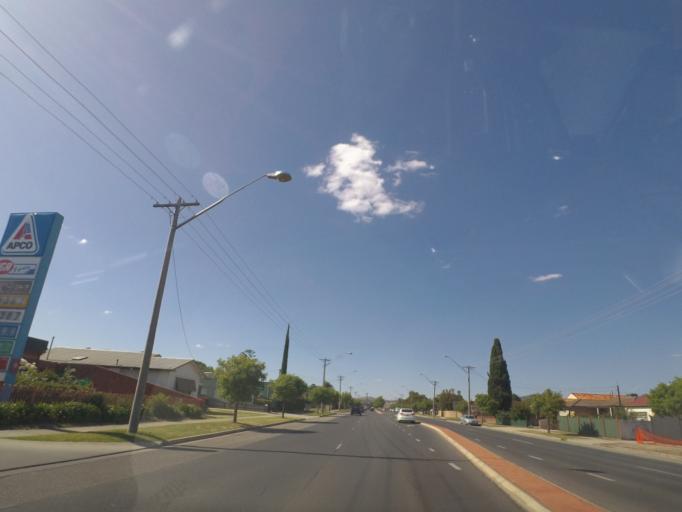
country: AU
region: New South Wales
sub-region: Albury Municipality
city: North Albury
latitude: -36.0573
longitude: 146.9326
